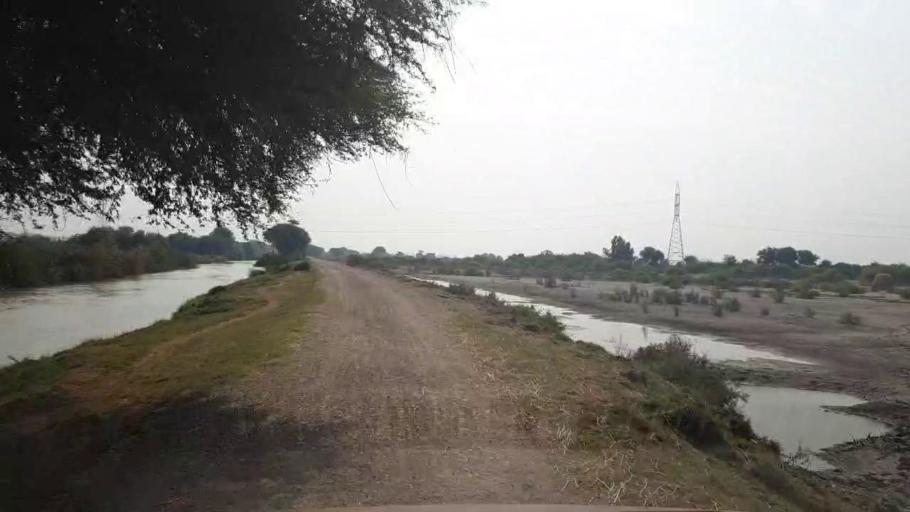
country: PK
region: Sindh
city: Tando Muhammad Khan
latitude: 25.1277
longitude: 68.4354
